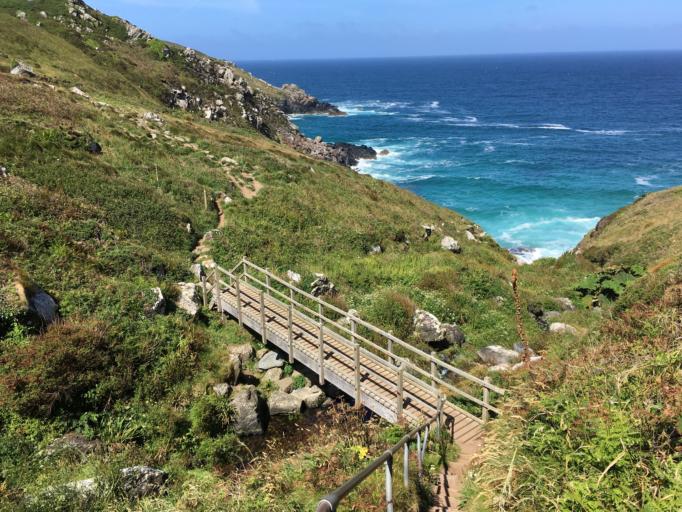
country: GB
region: England
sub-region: Cornwall
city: Penzance
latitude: 50.1950
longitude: -5.5756
